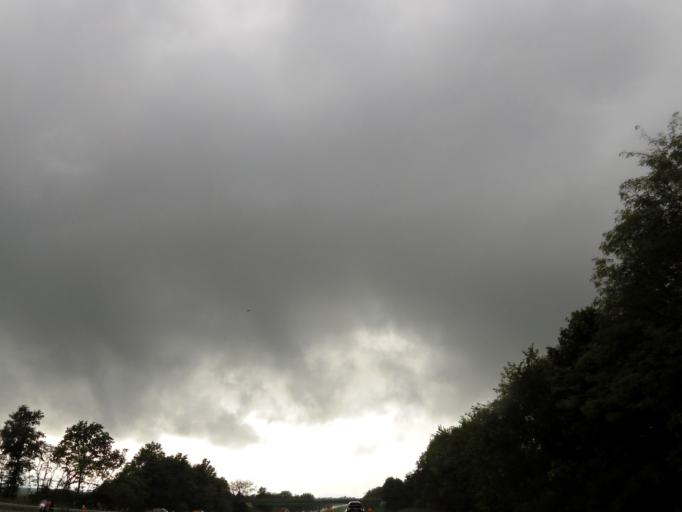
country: US
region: Illinois
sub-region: Jefferson County
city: Mount Vernon
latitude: 38.3414
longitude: -88.9666
